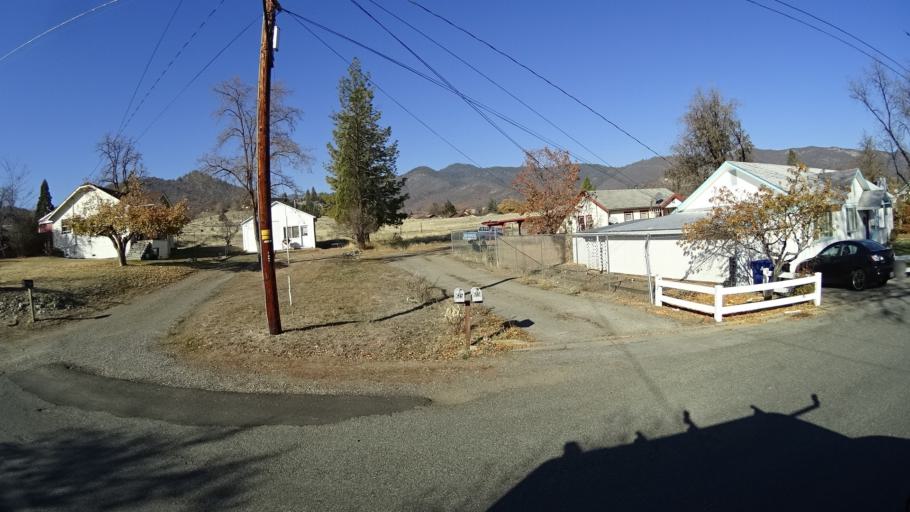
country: US
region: California
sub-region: Siskiyou County
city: Yreka
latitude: 41.7284
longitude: -122.6470
